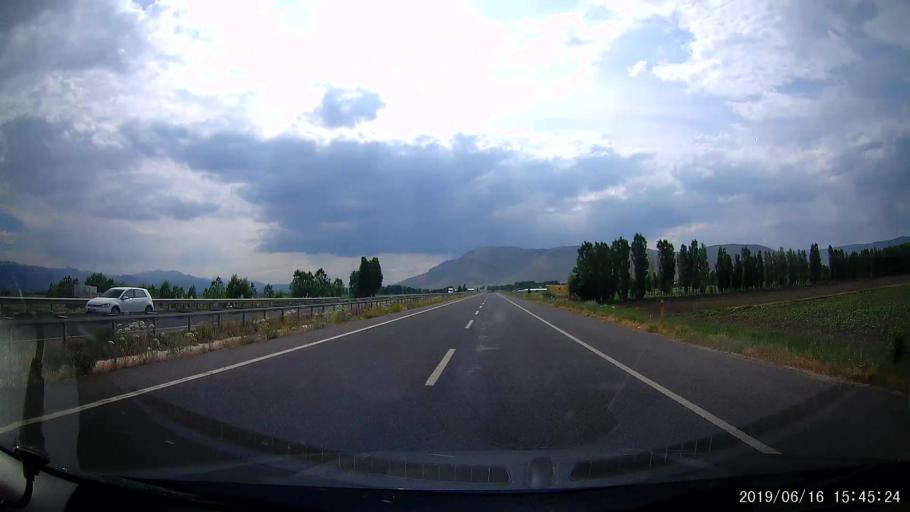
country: TR
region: Erzurum
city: Pasinler
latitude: 39.9885
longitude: 41.7671
